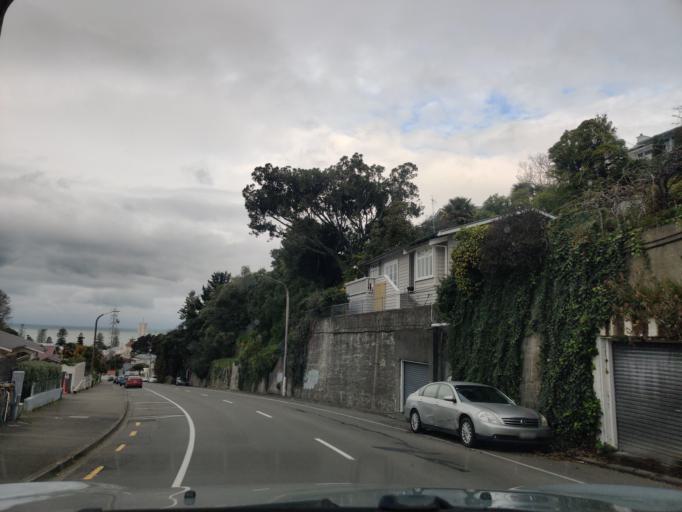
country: NZ
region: Hawke's Bay
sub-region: Napier City
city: Napier
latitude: -39.4867
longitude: 176.9127
